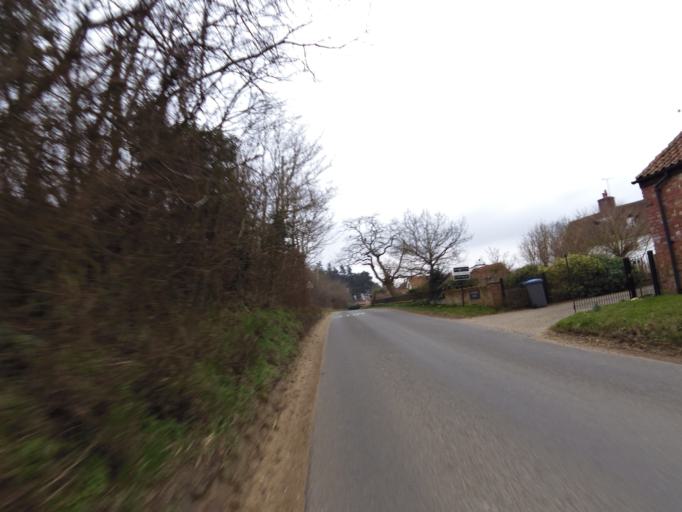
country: GB
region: England
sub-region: Suffolk
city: Wickham Market
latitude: 52.1712
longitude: 1.3491
